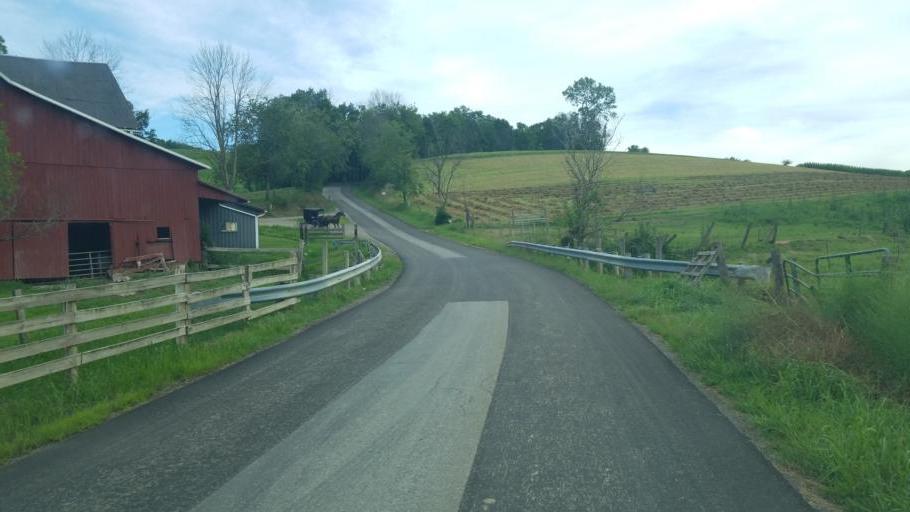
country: US
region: Ohio
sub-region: Holmes County
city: Millersburg
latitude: 40.5008
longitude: -81.8301
